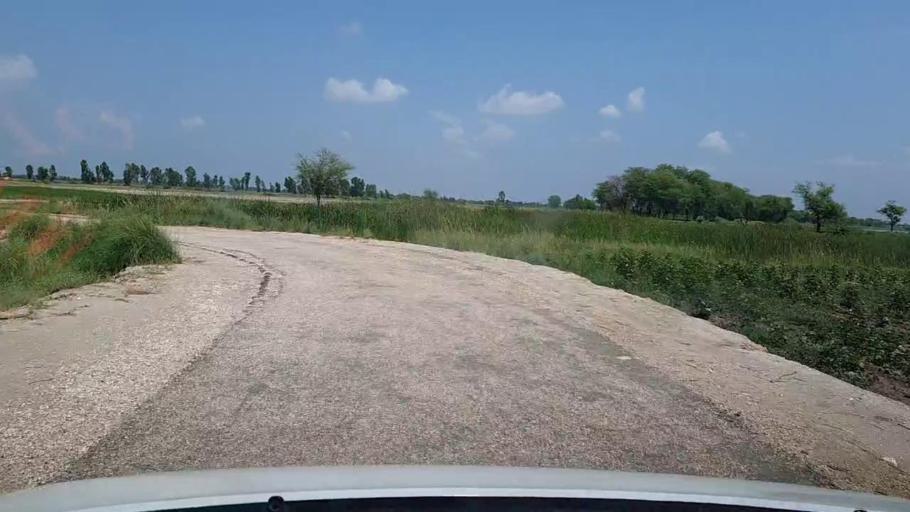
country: PK
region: Sindh
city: Bhiria
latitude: 26.9758
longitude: 68.2141
